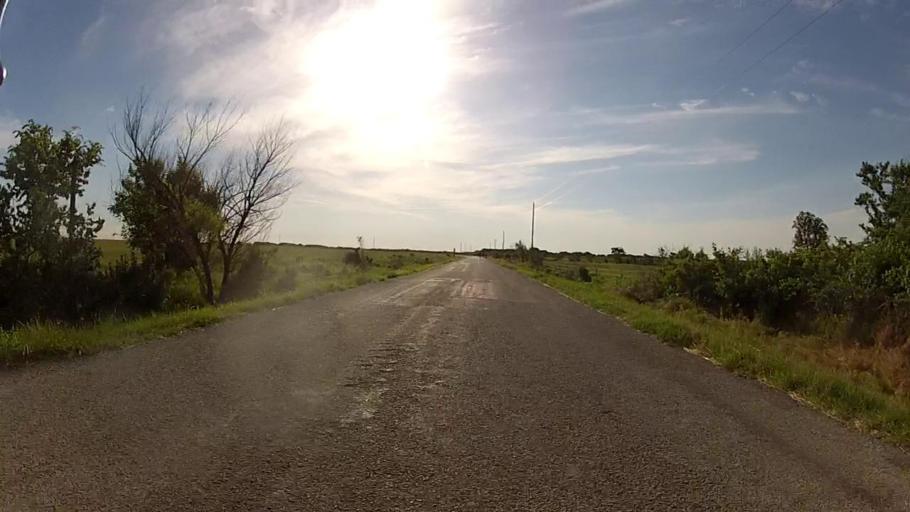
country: US
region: Kansas
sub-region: Cowley County
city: Arkansas City
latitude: 37.0486
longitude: -96.8263
